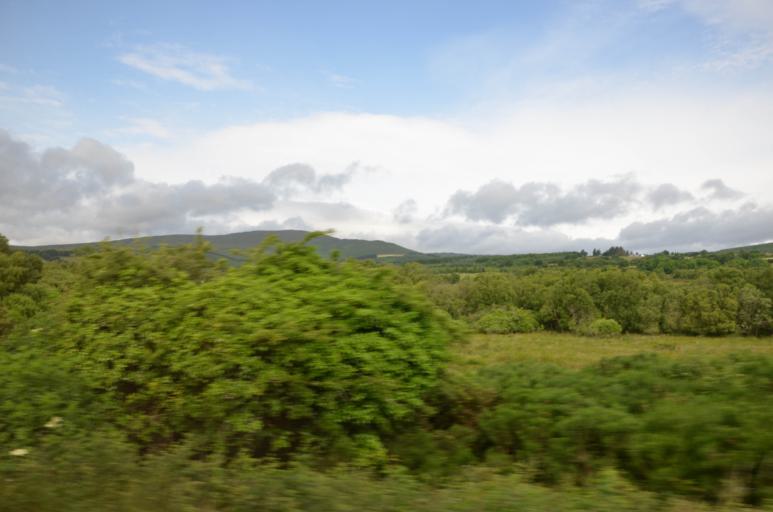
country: IE
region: Leinster
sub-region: Wicklow
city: Rathdrum
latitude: 53.0493
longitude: -6.2402
